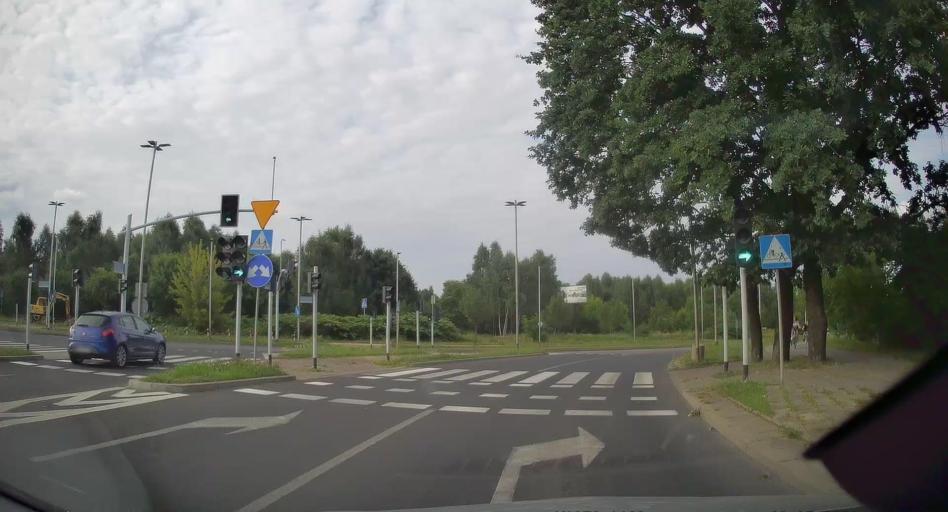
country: PL
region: Silesian Voivodeship
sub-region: Czestochowa
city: Czestochowa
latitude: 50.8229
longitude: 19.0885
